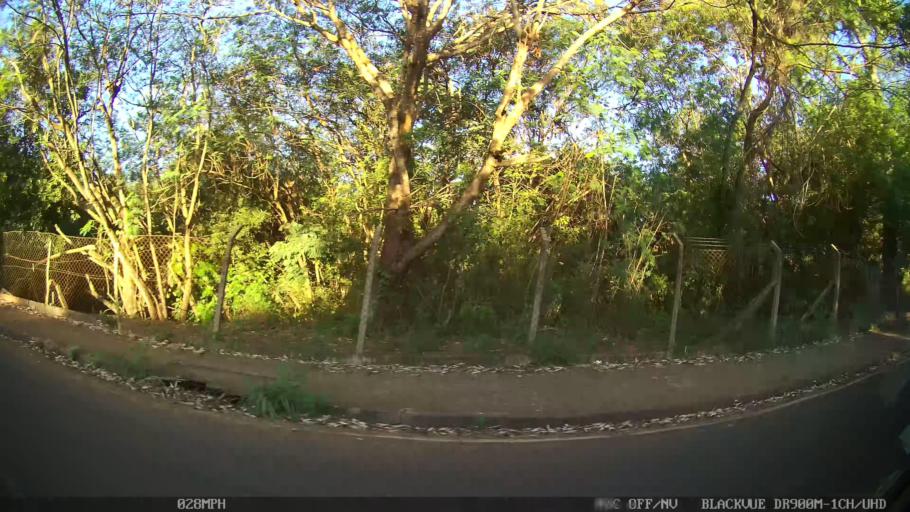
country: BR
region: Sao Paulo
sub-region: Sao Jose Do Rio Preto
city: Sao Jose do Rio Preto
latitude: -20.7746
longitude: -49.3552
